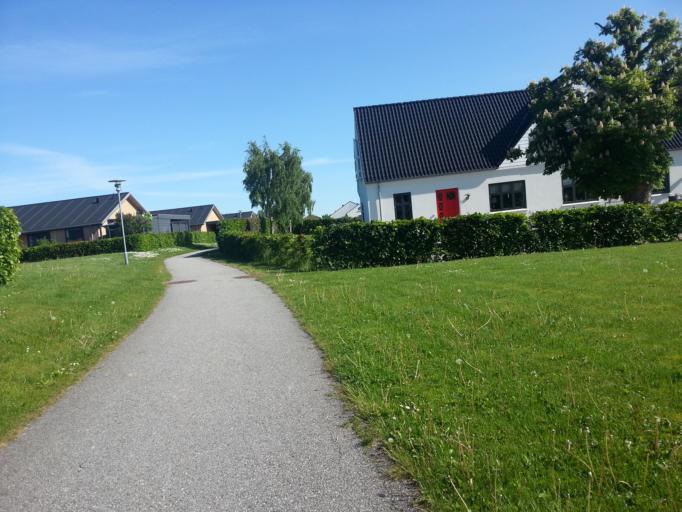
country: DK
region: North Denmark
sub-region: Alborg Kommune
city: Vadum
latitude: 57.1207
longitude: 9.8651
